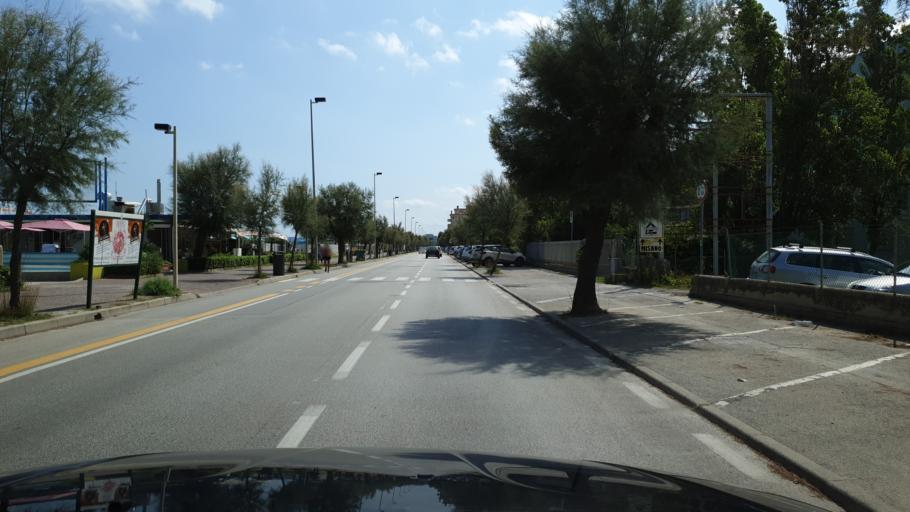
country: IT
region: Emilia-Romagna
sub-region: Provincia di Rimini
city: Misano Adriatico
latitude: 43.9881
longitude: 12.6842
